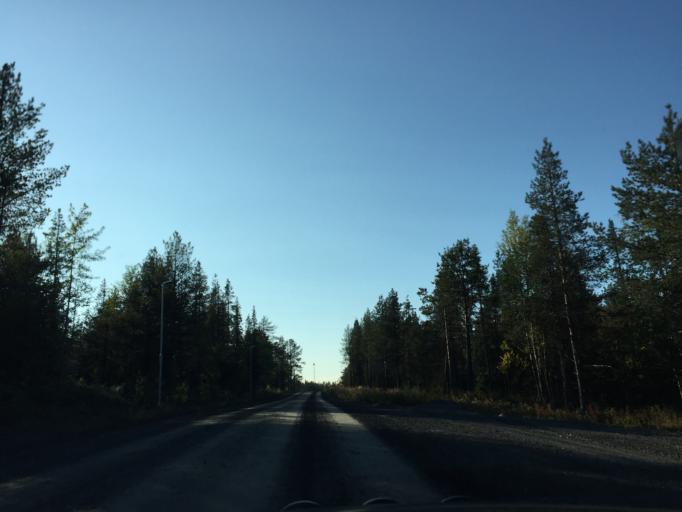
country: SE
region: Norrbotten
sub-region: Gallivare Kommun
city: Malmberget
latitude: 67.6435
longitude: 21.0283
